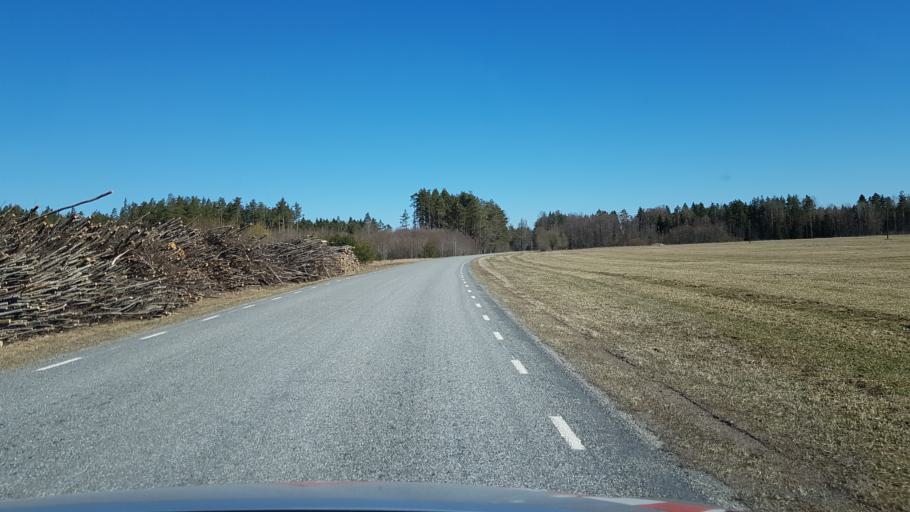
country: EE
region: Laeaene-Virumaa
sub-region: Haljala vald
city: Haljala
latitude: 59.4703
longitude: 26.2433
